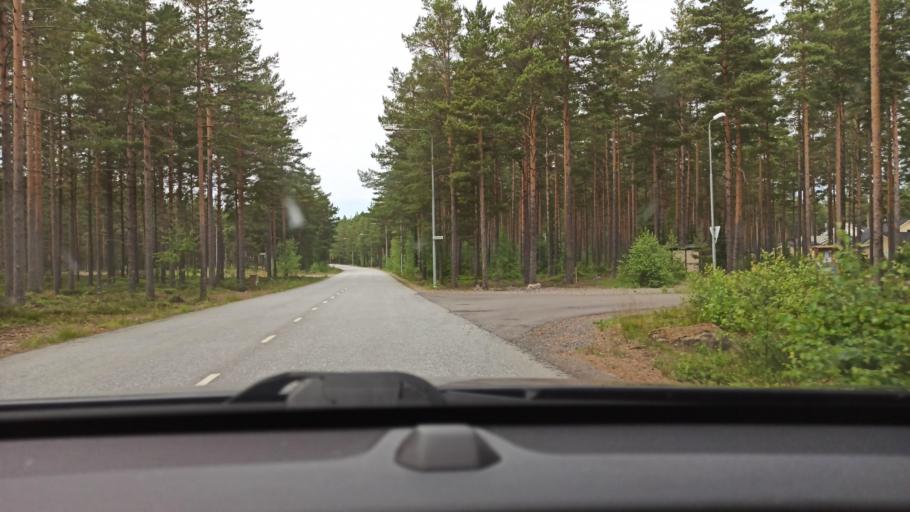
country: FI
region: Satakunta
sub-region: Pori
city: Luvia
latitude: 61.5730
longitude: 21.5308
